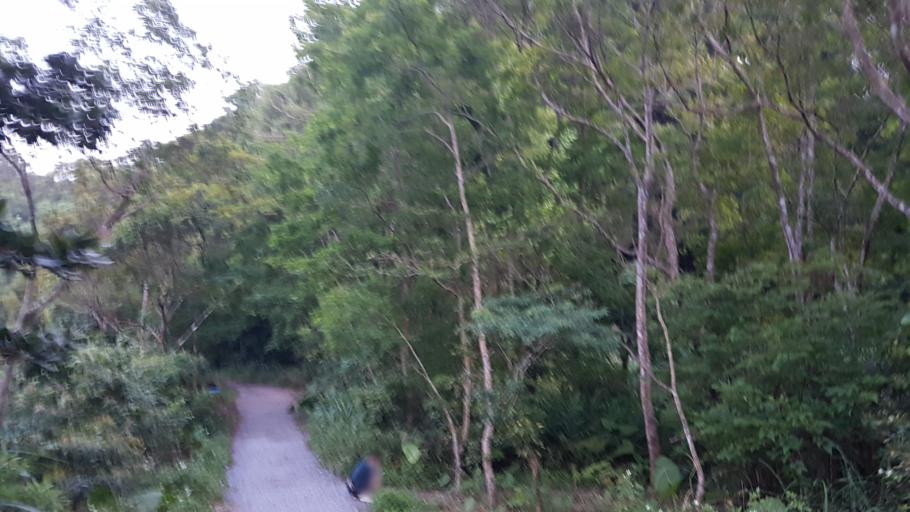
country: TW
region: Taiwan
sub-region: Yilan
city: Yilan
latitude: 24.9339
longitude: 121.7055
